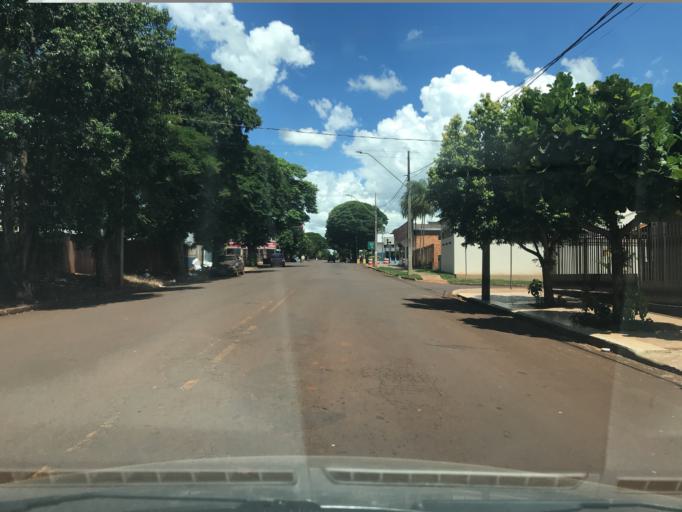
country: BR
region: Parana
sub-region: Palotina
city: Palotina
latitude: -24.2842
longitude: -53.8471
